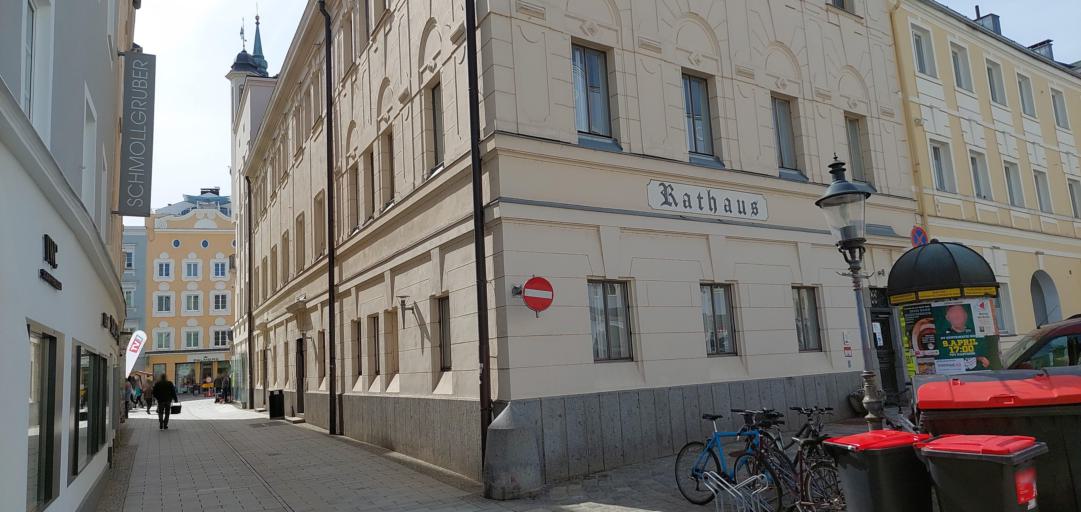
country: AT
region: Upper Austria
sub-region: Politischer Bezirk Ried im Innkreis
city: Ried im Innkreis
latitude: 48.2105
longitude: 13.4881
